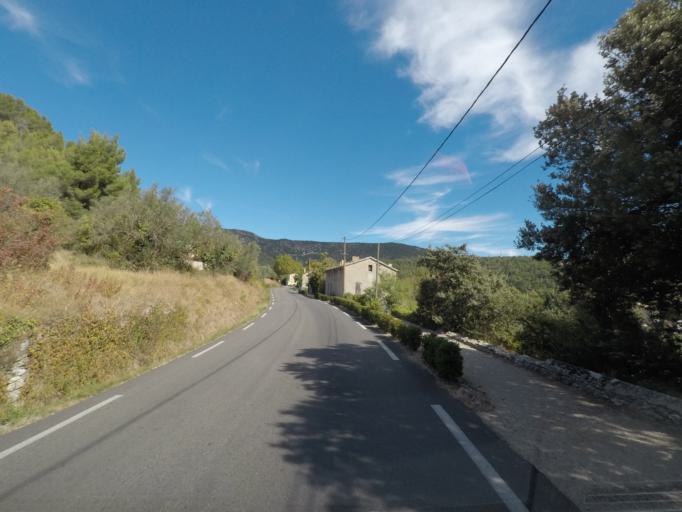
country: FR
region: Rhone-Alpes
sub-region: Departement de la Drome
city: Nyons
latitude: 44.3746
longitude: 5.1659
